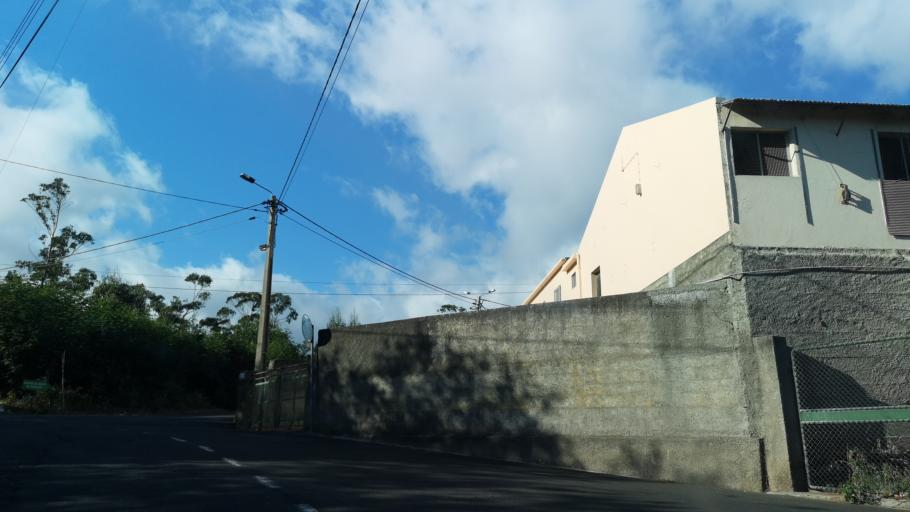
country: PT
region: Madeira
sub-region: Santa Cruz
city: Camacha
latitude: 32.6618
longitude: -16.8359
